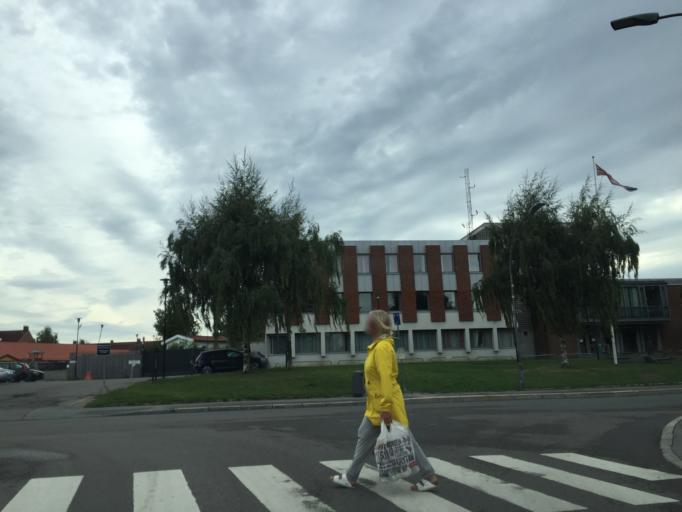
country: NO
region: Oslo
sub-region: Oslo
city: Oslo
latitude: 59.8968
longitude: 10.8141
